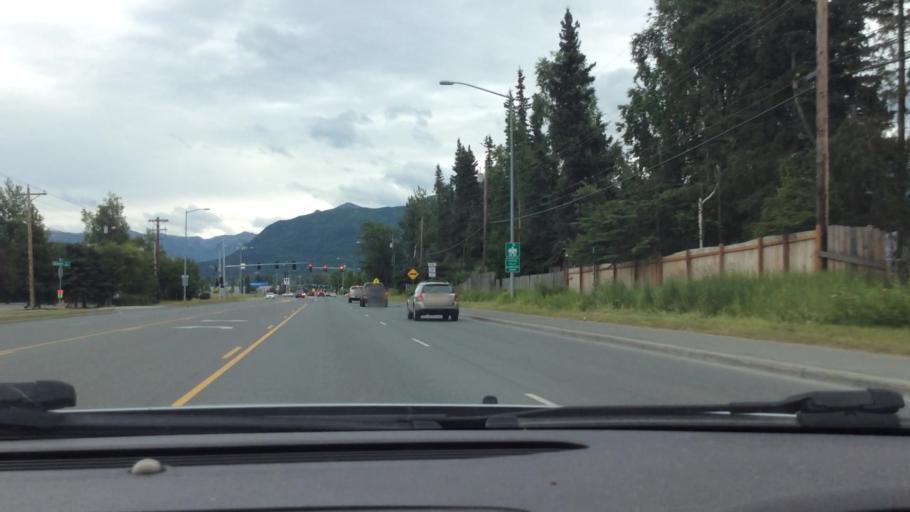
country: US
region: Alaska
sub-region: Anchorage Municipality
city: Elmendorf Air Force Base
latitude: 61.2098
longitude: -149.7520
